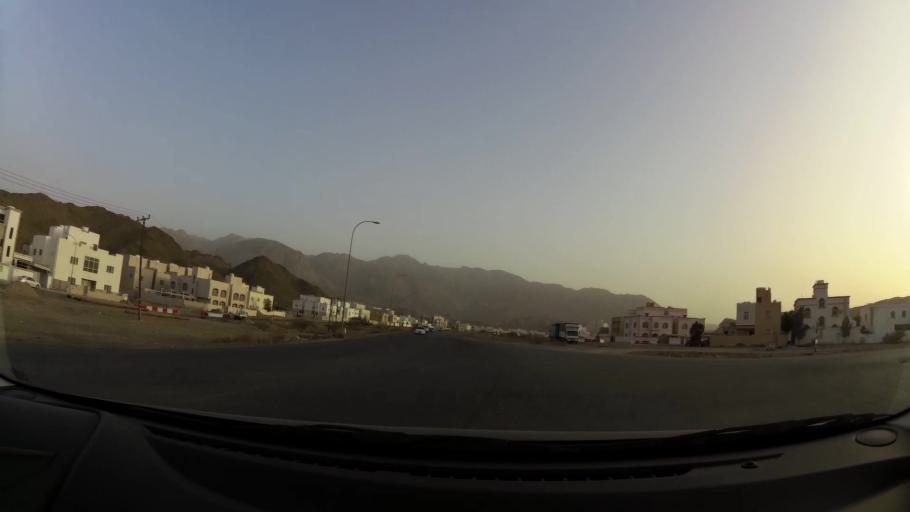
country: OM
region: Muhafazat Masqat
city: Bawshar
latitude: 23.4871
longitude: 58.3137
